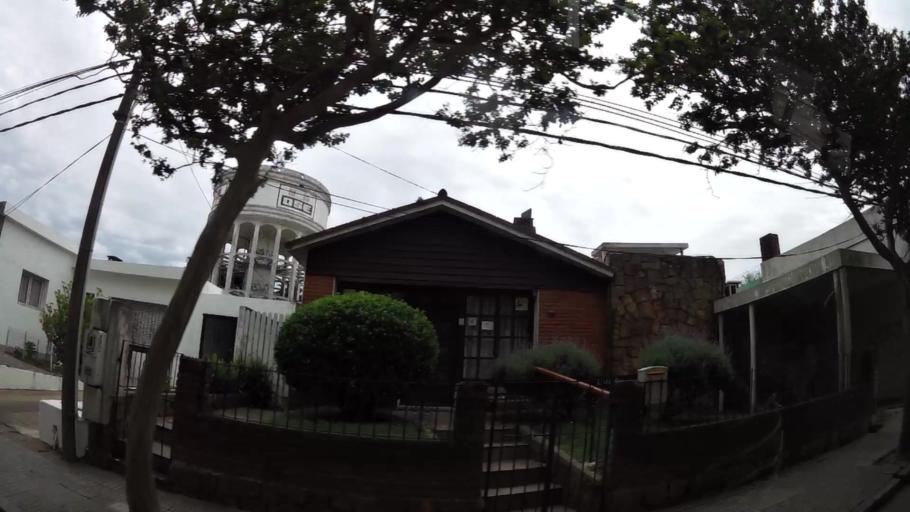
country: UY
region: Maldonado
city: Maldonado
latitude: -34.9111
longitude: -54.9576
